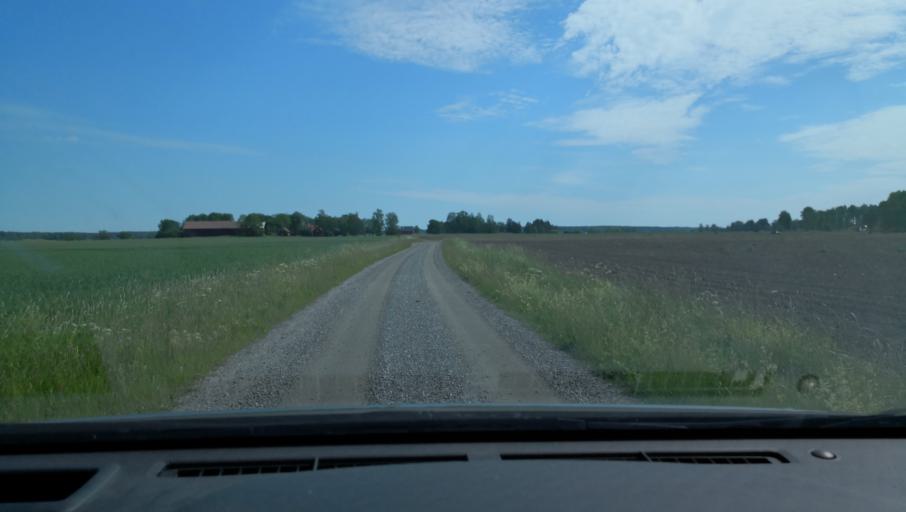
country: SE
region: Uppsala
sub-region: Enkopings Kommun
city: Enkoping
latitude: 59.7033
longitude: 17.1315
